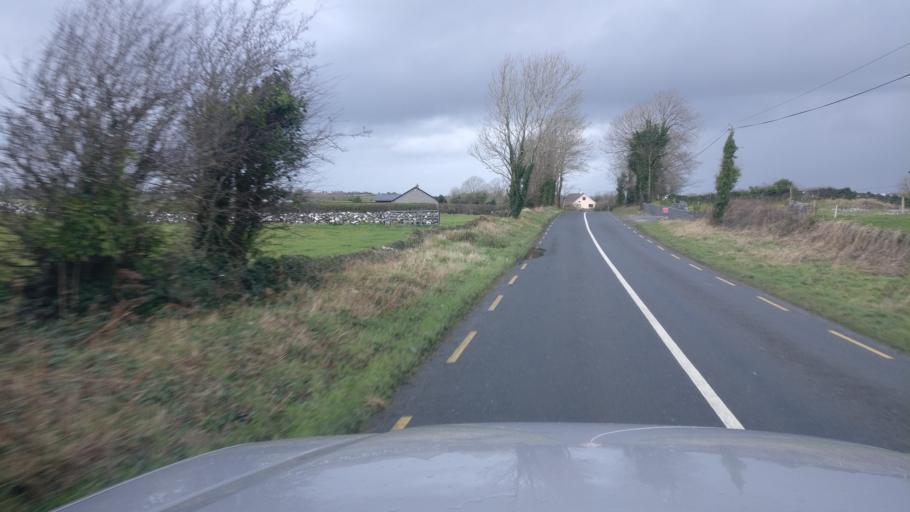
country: IE
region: Connaught
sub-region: County Galway
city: Loughrea
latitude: 53.1698
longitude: -8.6802
